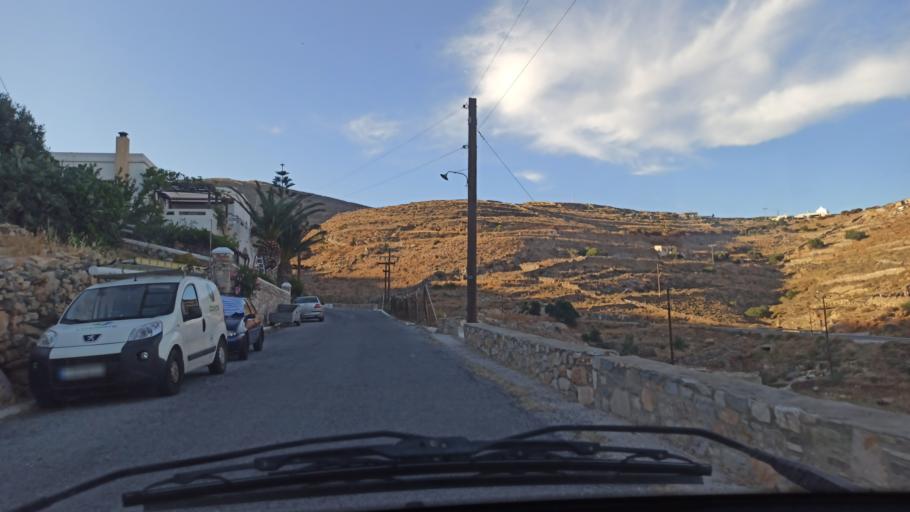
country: GR
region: South Aegean
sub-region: Nomos Kykladon
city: Ano Syros
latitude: 37.4497
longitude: 24.9375
